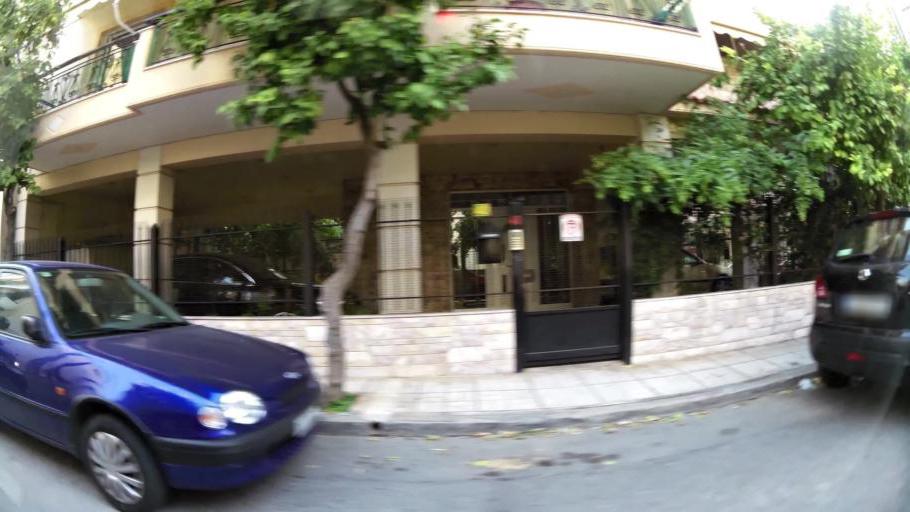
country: GR
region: Attica
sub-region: Nomarchia Athinas
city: Peristeri
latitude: 38.0211
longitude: 23.6902
